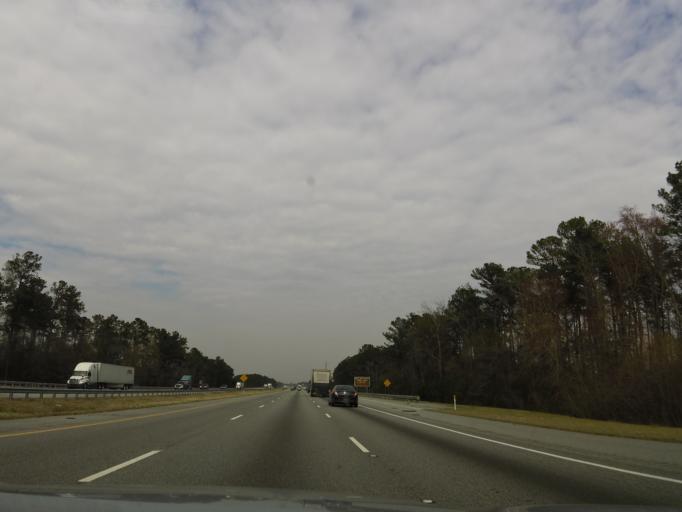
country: US
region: Georgia
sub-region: Liberty County
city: Midway
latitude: 31.6401
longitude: -81.4016
